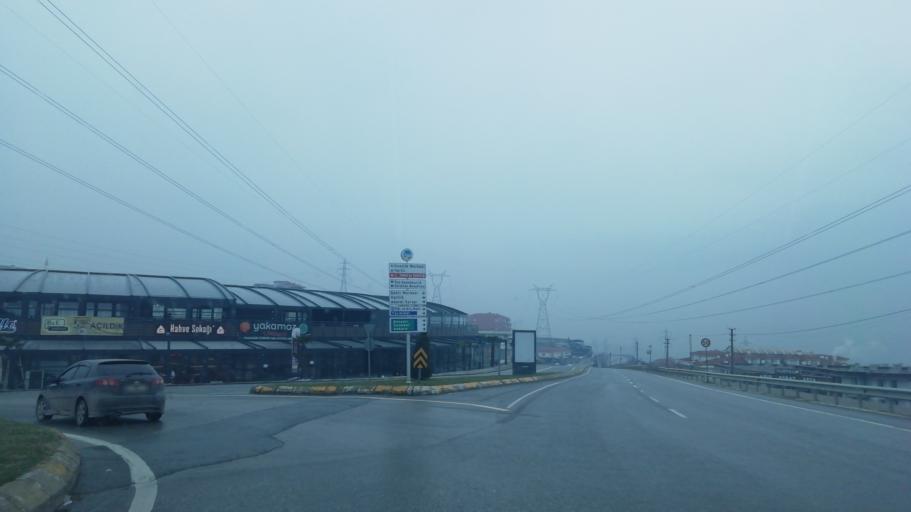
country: TR
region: Sakarya
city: Adapazari
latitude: 40.7477
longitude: 30.3523
